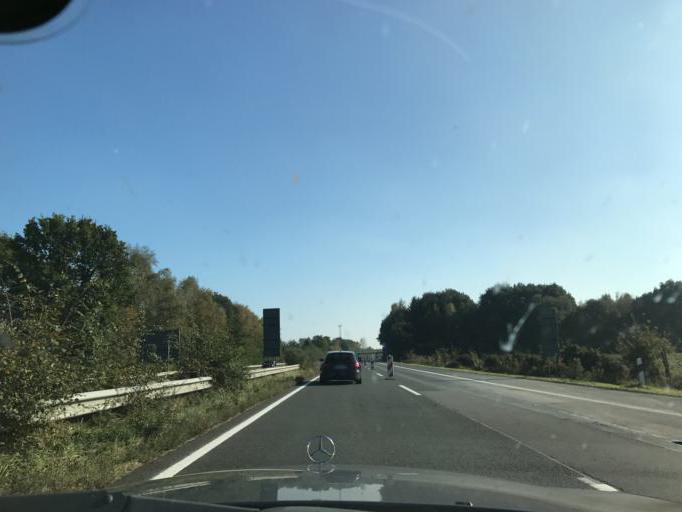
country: DE
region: Lower Saxony
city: Wiefelstede
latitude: 53.1973
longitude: 8.0947
